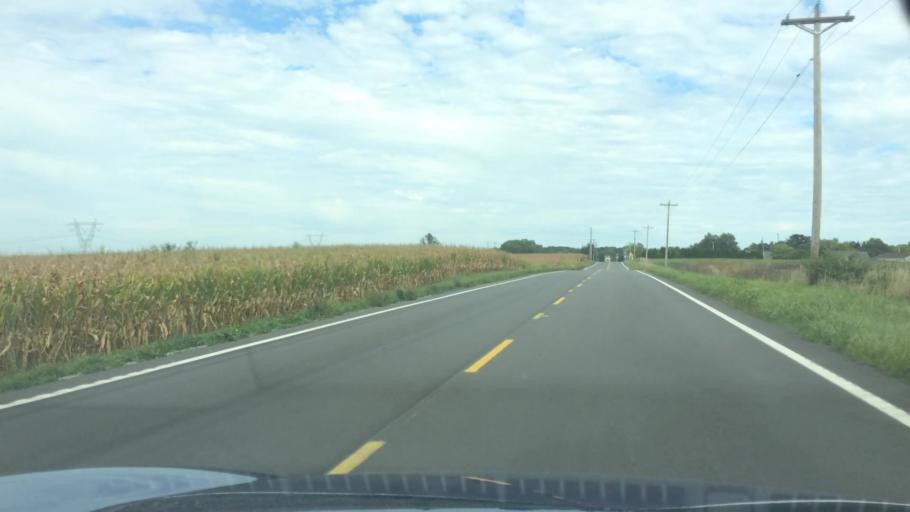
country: US
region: Ohio
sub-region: Logan County
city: Russells Point
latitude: 40.4464
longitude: -83.8133
